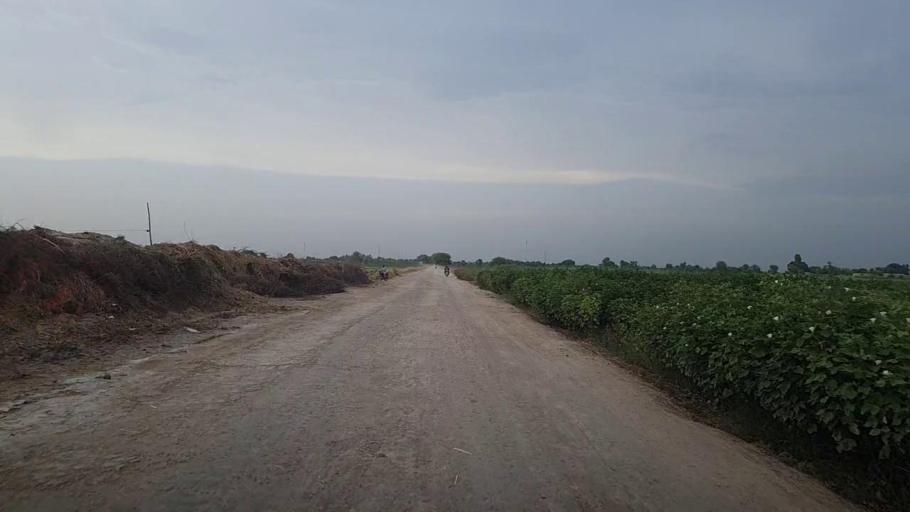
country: PK
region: Sindh
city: Karaundi
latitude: 26.9686
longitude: 68.3438
